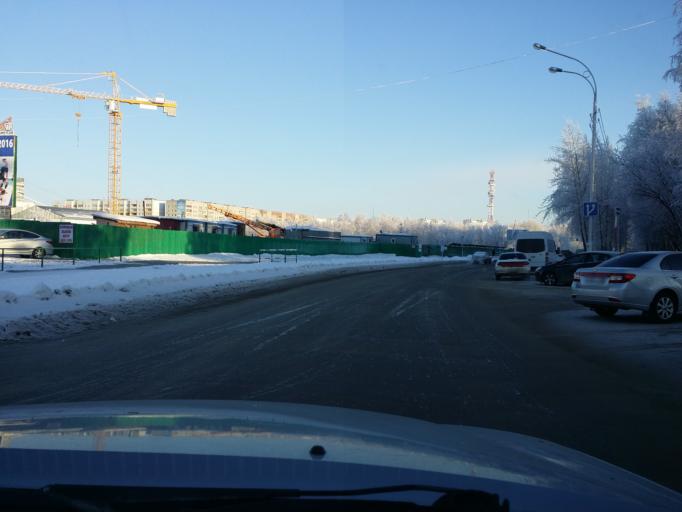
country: RU
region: Khanty-Mansiyskiy Avtonomnyy Okrug
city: Nizhnevartovsk
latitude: 60.9375
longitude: 76.5536
